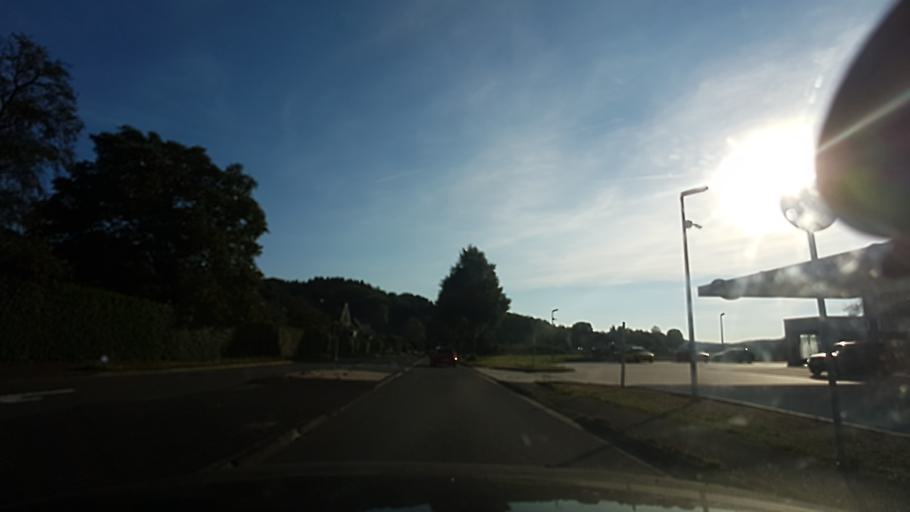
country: DE
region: North Rhine-Westphalia
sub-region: Regierungsbezirk Koln
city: Marienheide
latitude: 51.0603
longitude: 7.5550
